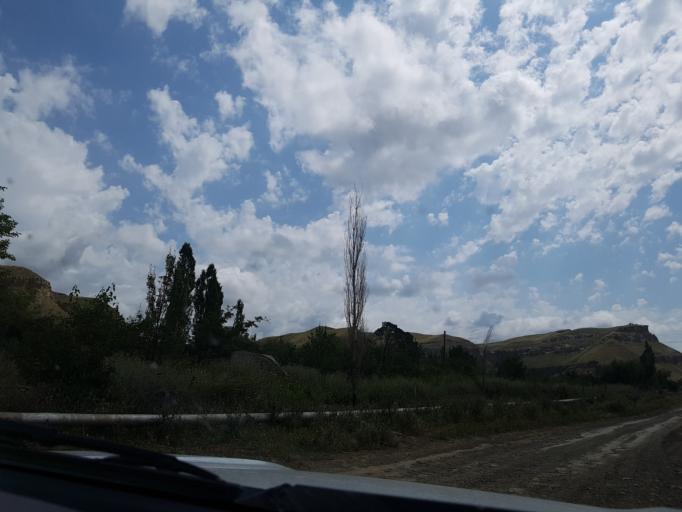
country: TM
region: Ahal
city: Baharly
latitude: 38.2233
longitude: 56.8925
